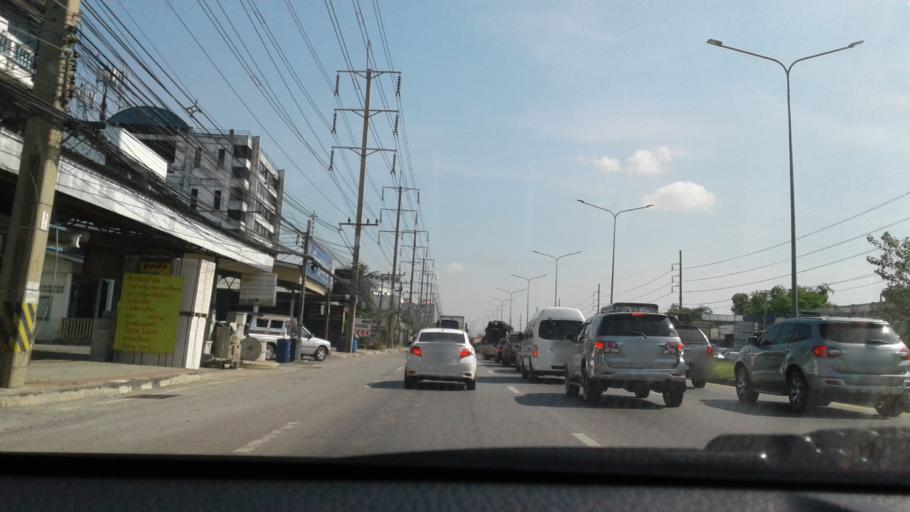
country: TH
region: Phra Nakhon Si Ayutthaya
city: Ban Bang Kadi Pathum Thani
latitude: 13.9760
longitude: 100.5815
